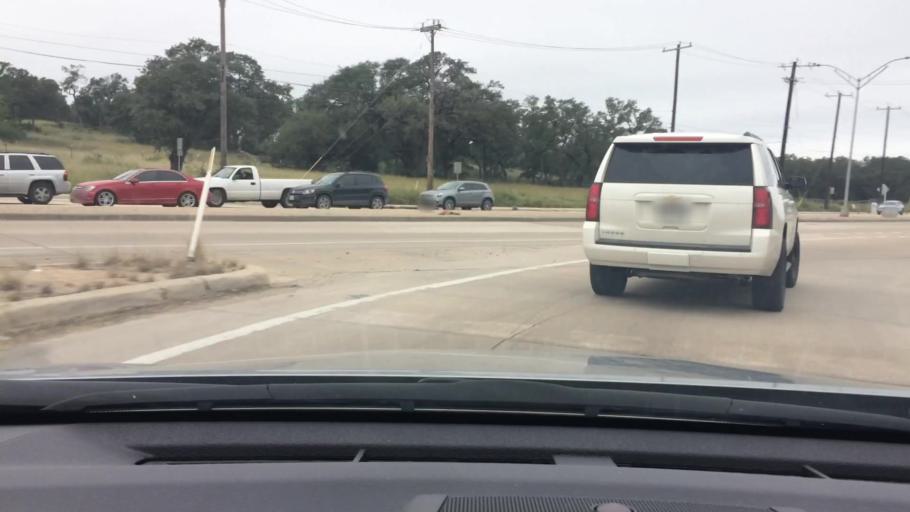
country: US
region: Texas
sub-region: Bexar County
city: Hollywood Park
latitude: 29.6014
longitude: -98.4182
